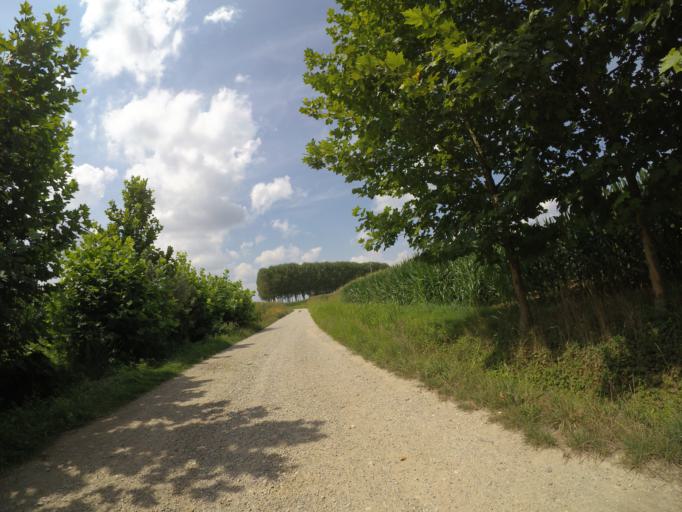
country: IT
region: Friuli Venezia Giulia
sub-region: Provincia di Udine
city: Rivignano
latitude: 45.8927
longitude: 13.0198
